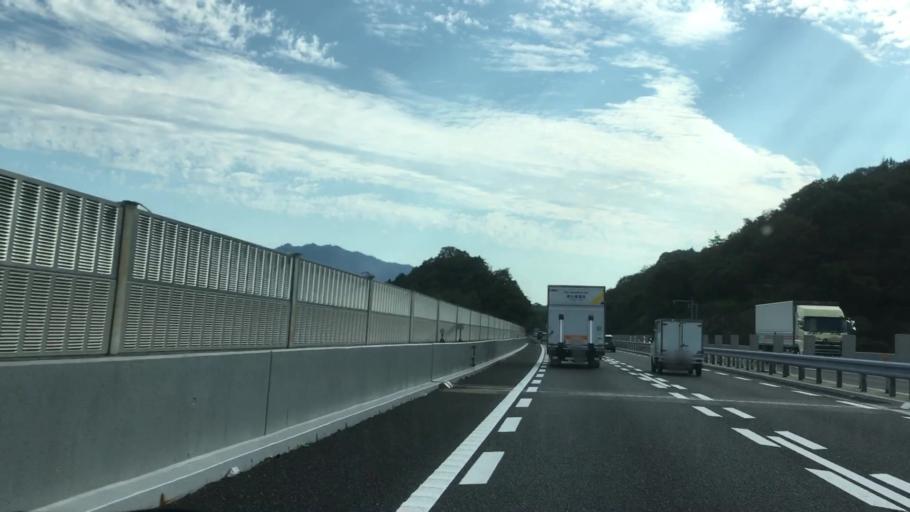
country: JP
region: Hiroshima
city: Ono-hara
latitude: 34.3129
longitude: 132.2806
